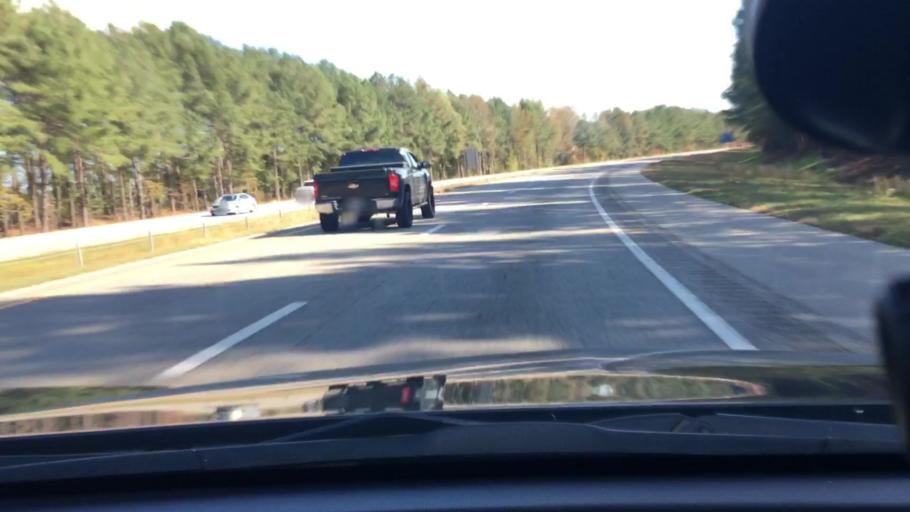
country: US
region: North Carolina
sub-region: Wilson County
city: Wilson
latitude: 35.6788
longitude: -77.8382
